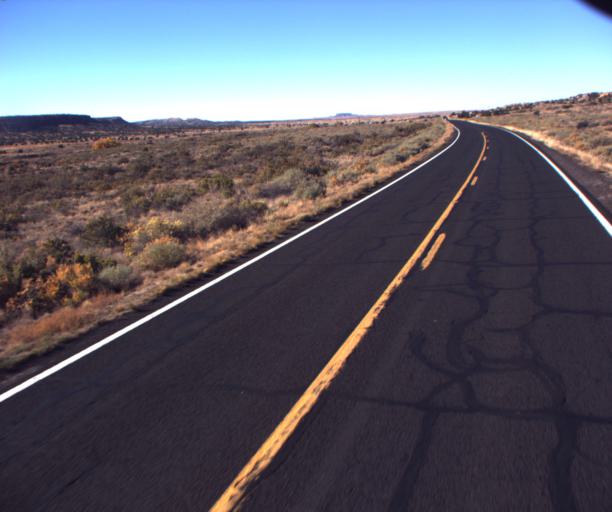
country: US
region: Arizona
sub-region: Navajo County
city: First Mesa
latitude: 35.8398
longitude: -110.2564
